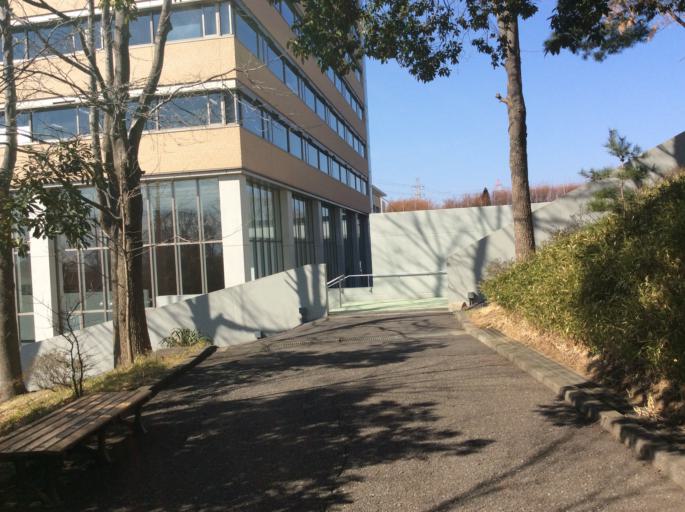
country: JP
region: Tokyo
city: Hino
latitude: 35.6442
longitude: 139.4087
